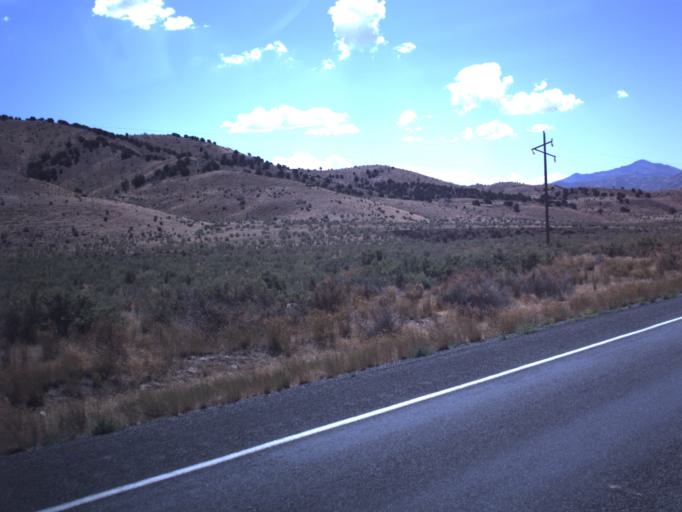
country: US
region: Utah
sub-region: Juab County
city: Nephi
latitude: 39.6151
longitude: -112.1307
